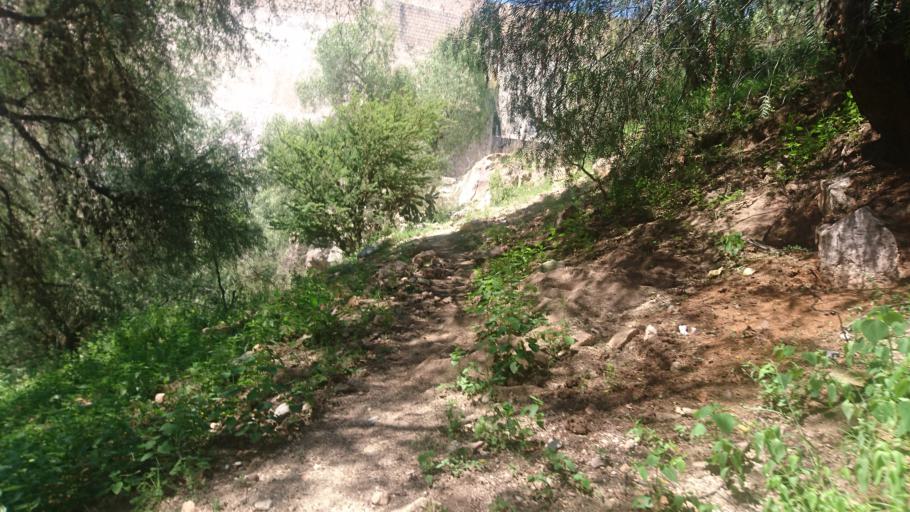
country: MX
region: San Luis Potosi
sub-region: Villa de Reyes
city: La Ventilla
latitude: 21.8194
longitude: -101.0275
